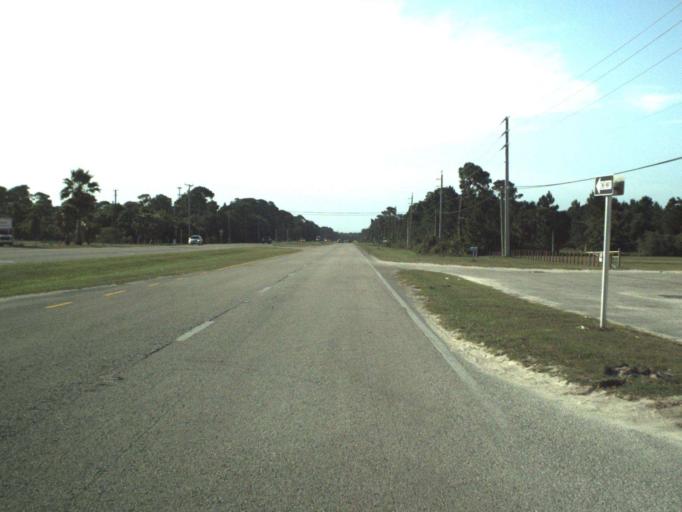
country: US
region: Florida
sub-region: Volusia County
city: Oak Hill
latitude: 28.8775
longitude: -80.8531
